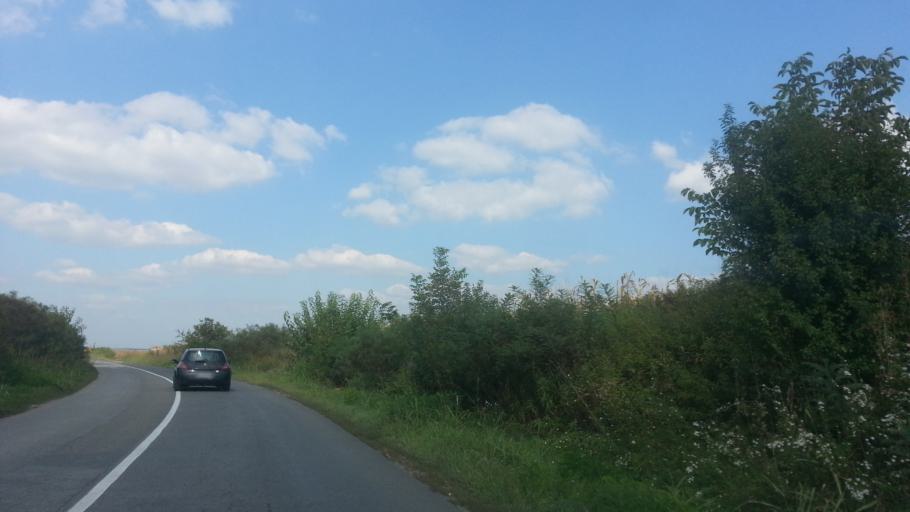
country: RS
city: Novi Banovci
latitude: 44.9221
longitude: 20.2815
